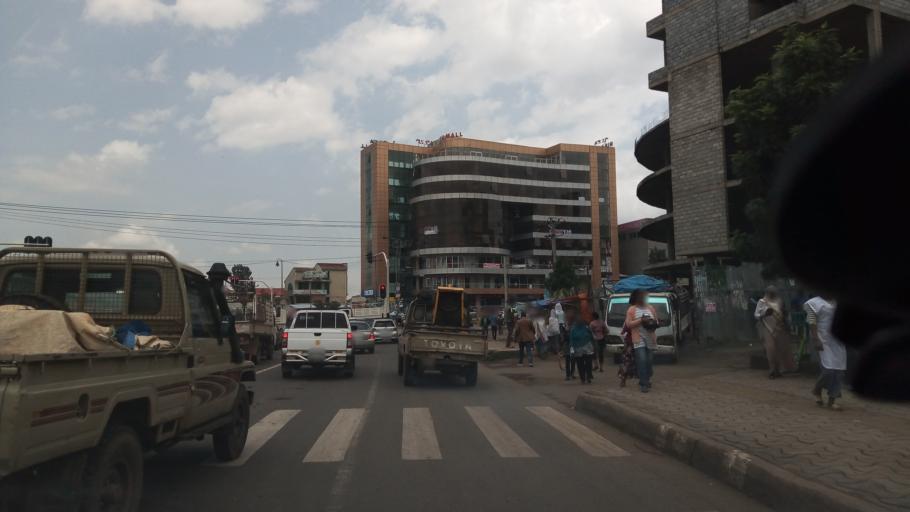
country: ET
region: Adis Abeba
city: Addis Ababa
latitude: 8.9695
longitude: 38.7223
